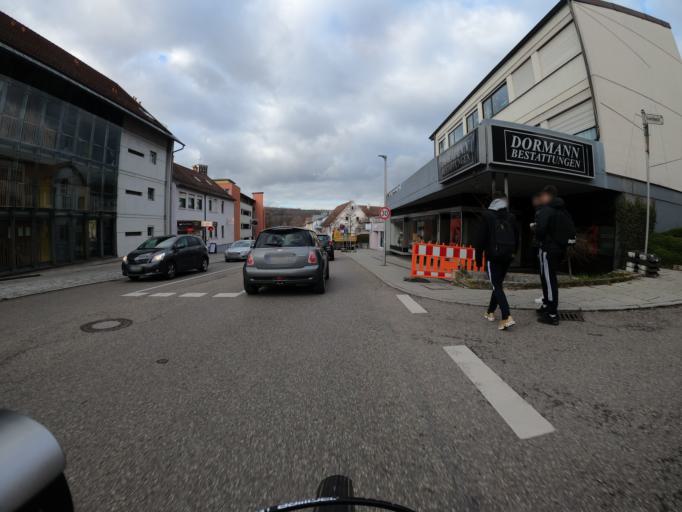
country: DE
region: Baden-Wuerttemberg
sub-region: Regierungsbezirk Stuttgart
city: Wernau
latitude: 48.6922
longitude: 9.4163
